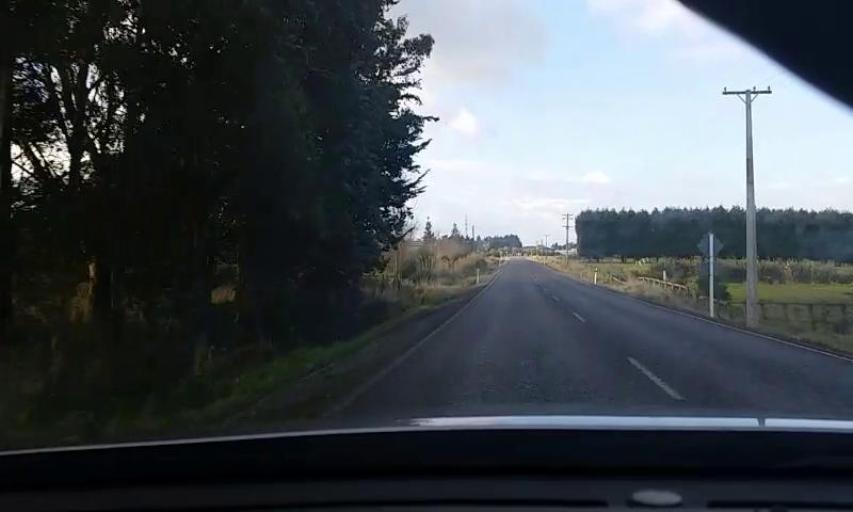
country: NZ
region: Southland
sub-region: Invercargill City
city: Invercargill
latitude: -46.3815
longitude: 168.4486
